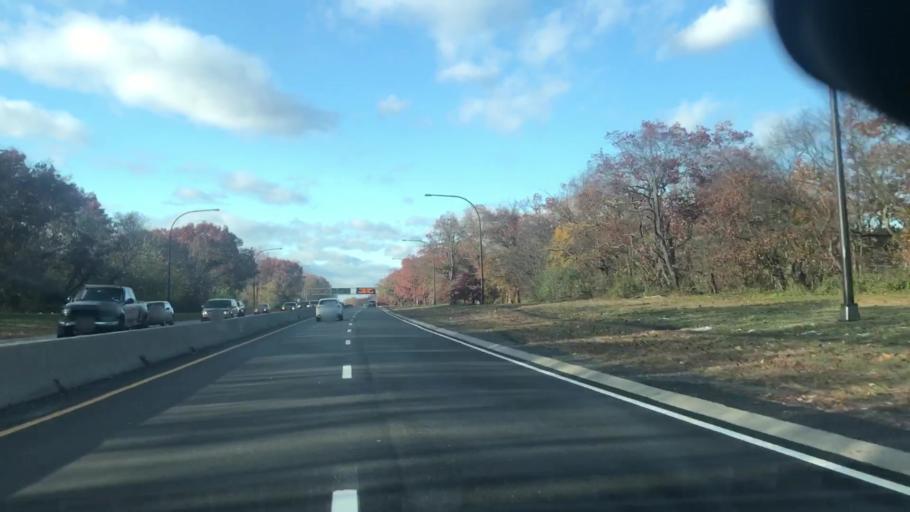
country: US
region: New York
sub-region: Nassau County
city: North Bellmore
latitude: 40.7086
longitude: -73.5267
